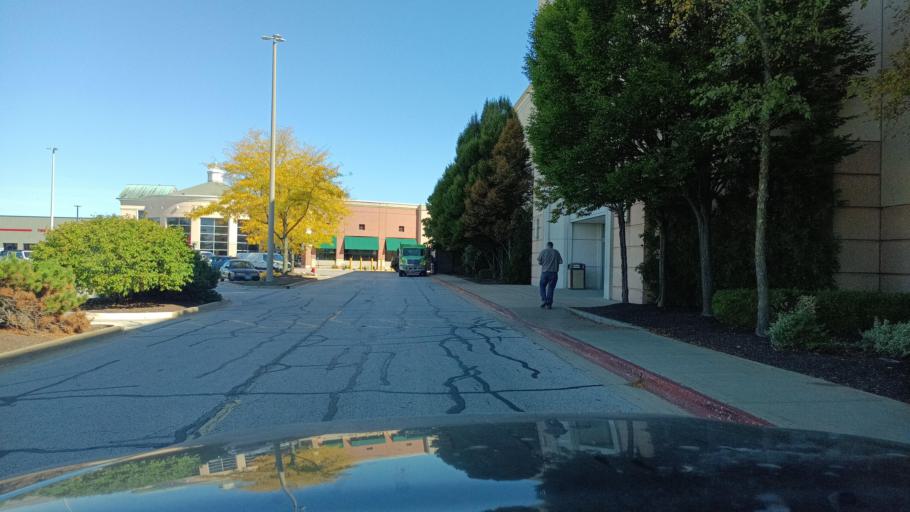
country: US
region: Illinois
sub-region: Champaign County
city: Champaign
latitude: 40.1410
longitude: -88.2448
